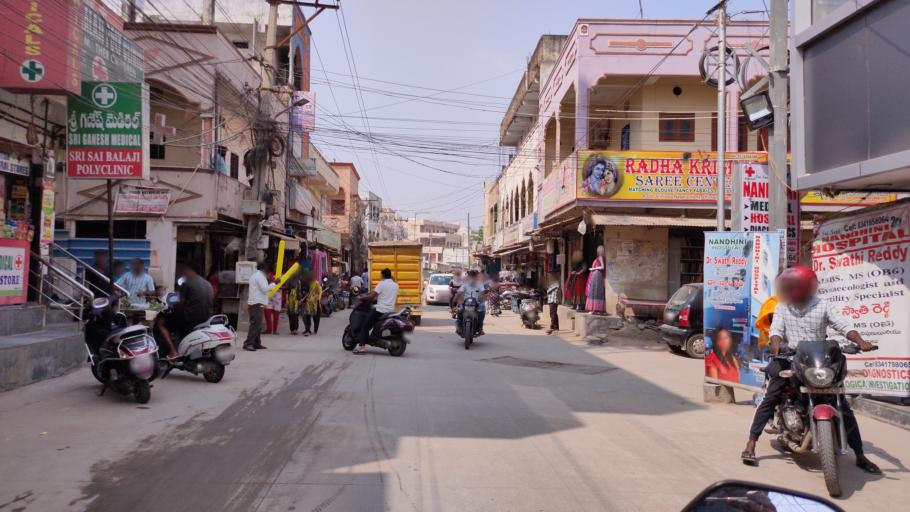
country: IN
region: Telangana
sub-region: Rangareddi
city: Quthbullapur
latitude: 17.4950
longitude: 78.4576
